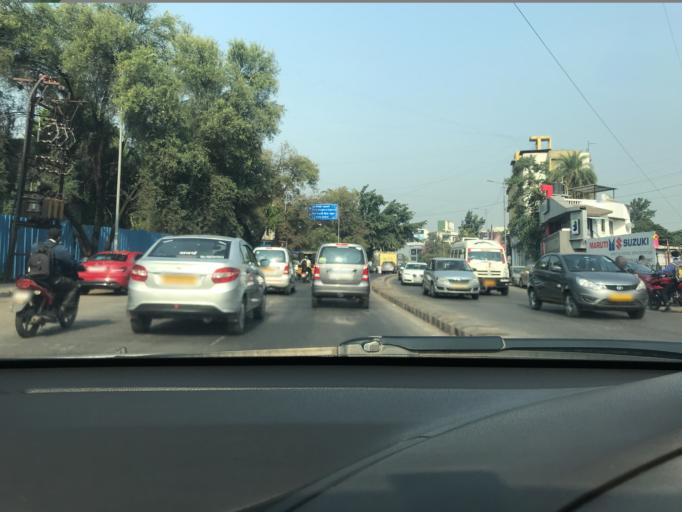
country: IN
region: Maharashtra
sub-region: Pune Division
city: Khadki
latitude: 18.5527
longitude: 73.8032
